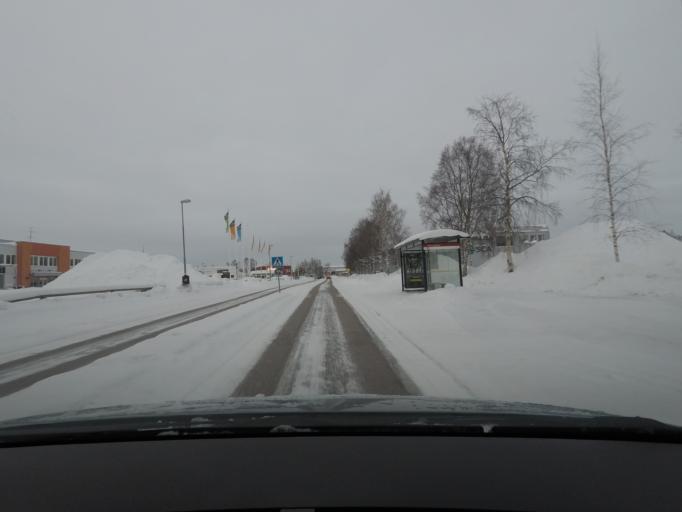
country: SE
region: Norrbotten
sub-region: Lulea Kommun
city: Lulea
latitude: 65.5978
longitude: 22.1453
